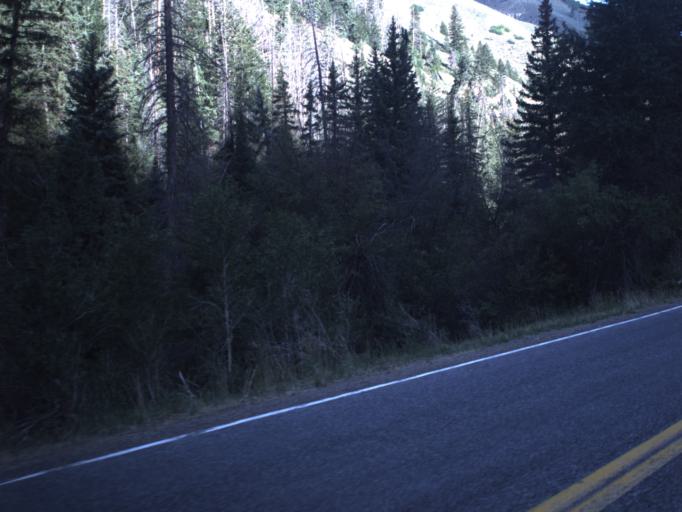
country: US
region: Utah
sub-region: Emery County
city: Huntington
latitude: 39.4679
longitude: -111.1517
